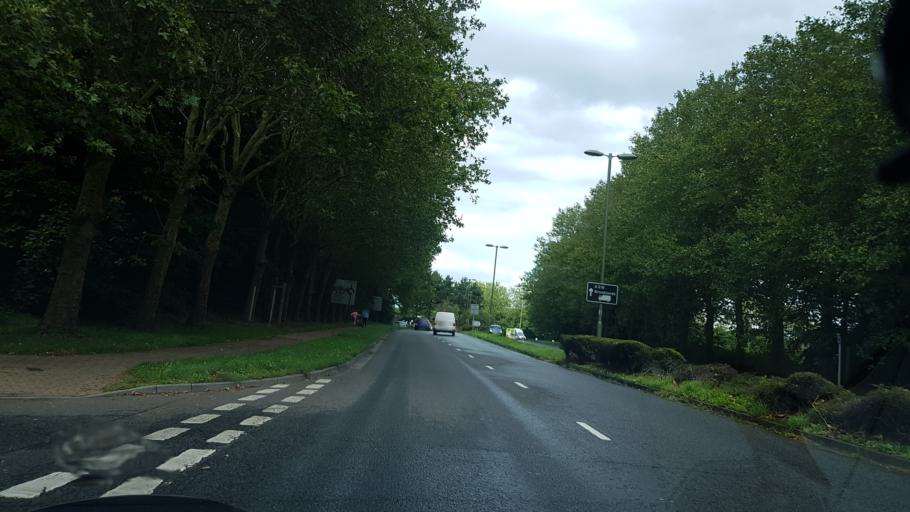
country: GB
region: England
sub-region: Surrey
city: Byfleet
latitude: 51.3417
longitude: -0.4725
